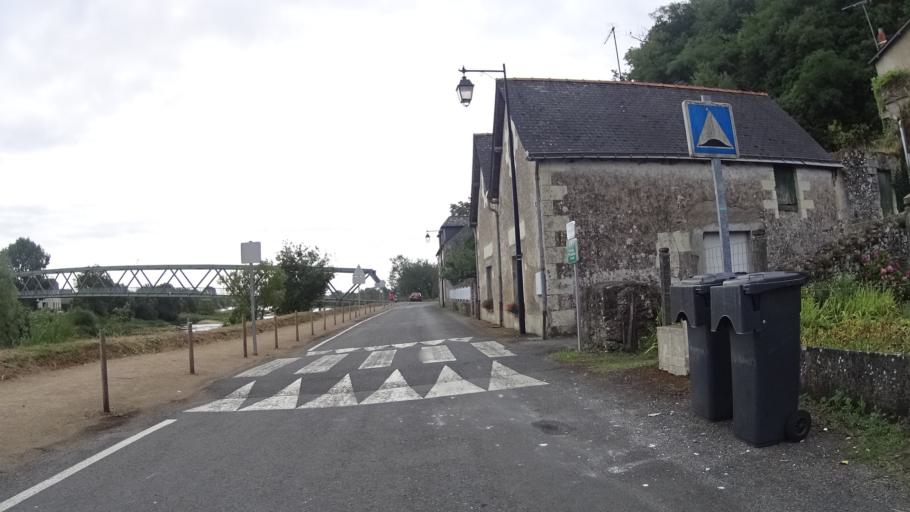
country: FR
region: Pays de la Loire
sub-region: Departement de Maine-et-Loire
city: Montjean-sur-Loire
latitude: 47.3872
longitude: -0.8513
